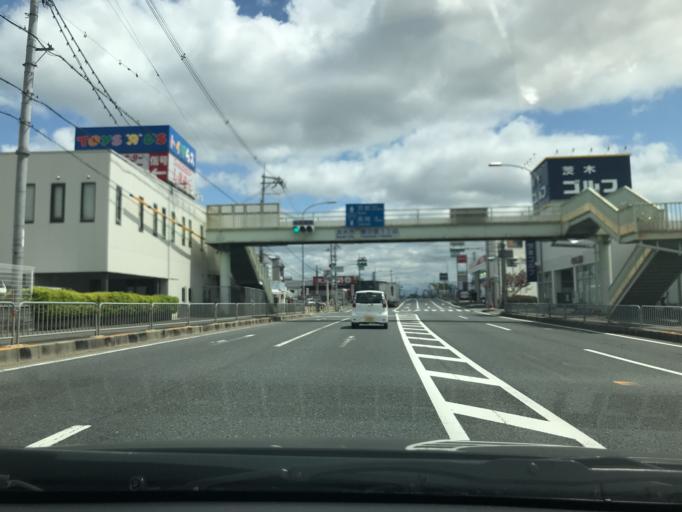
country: JP
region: Osaka
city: Ibaraki
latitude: 34.8368
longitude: 135.5448
